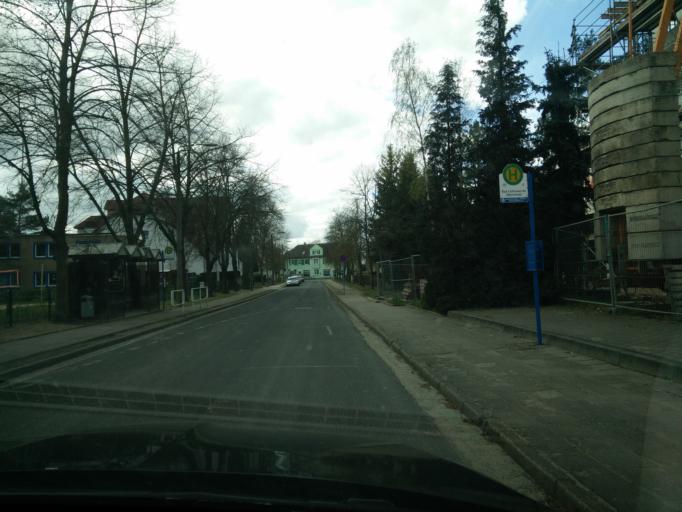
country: DE
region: Brandenburg
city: Bad Liebenwerda
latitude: 51.5270
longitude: 13.3997
